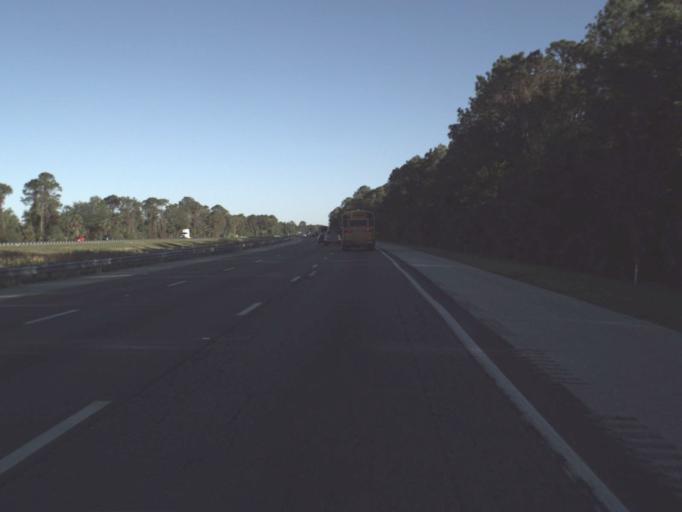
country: US
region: Florida
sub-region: Flagler County
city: Flagler Beach
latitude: 29.4286
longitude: -81.1665
